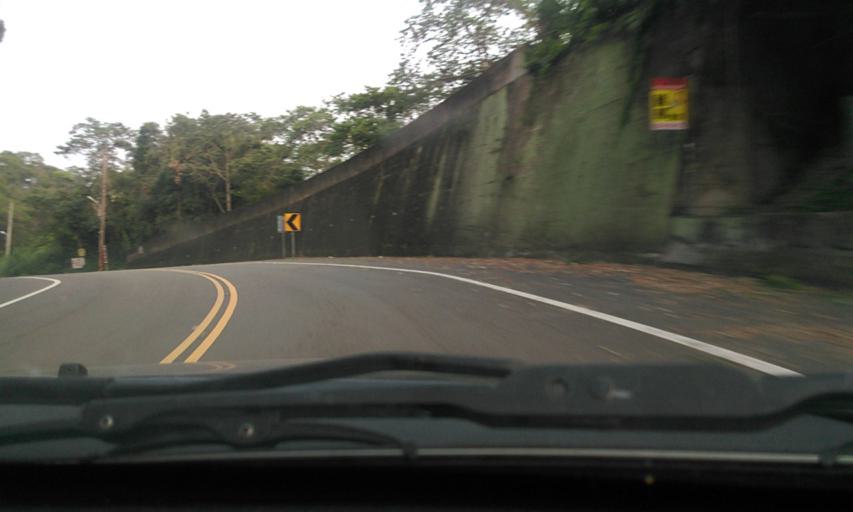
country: TW
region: Taiwan
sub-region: Hsinchu
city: Hsinchu
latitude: 24.6863
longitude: 120.9779
